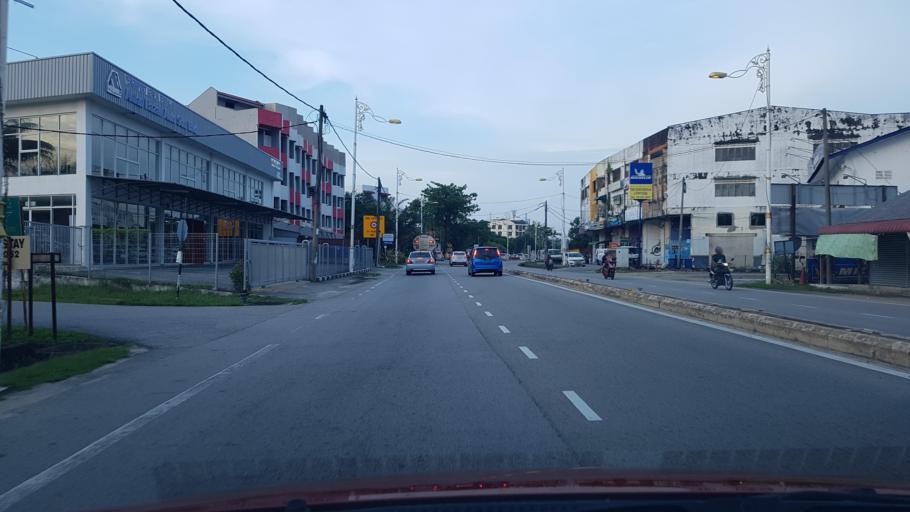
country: MY
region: Terengganu
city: Kuala Terengganu
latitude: 5.3148
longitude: 103.1477
